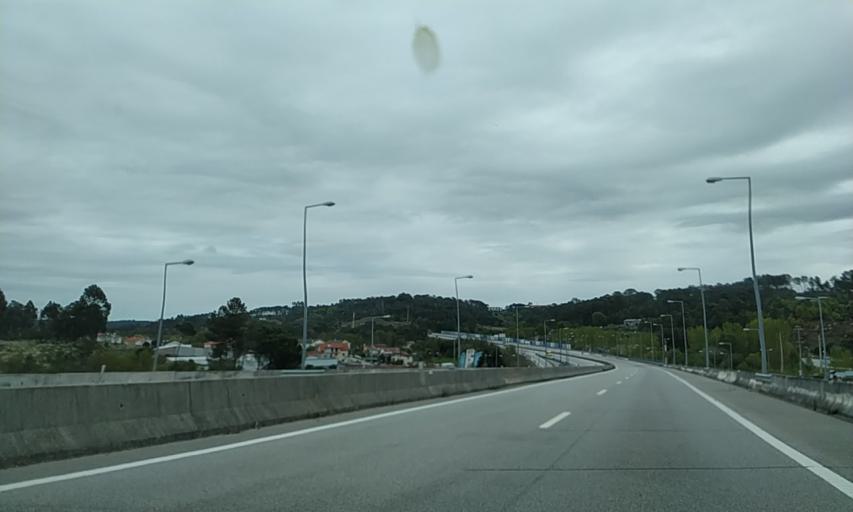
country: PT
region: Viseu
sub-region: Viseu
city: Viseu
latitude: 40.6229
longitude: -7.9211
